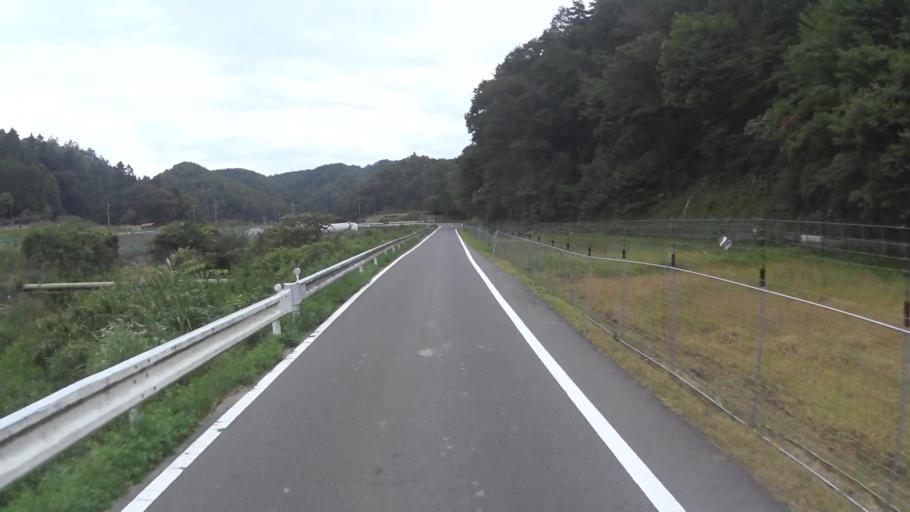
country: JP
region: Mie
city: Ueno-ebisumachi
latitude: 34.8285
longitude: 135.9719
